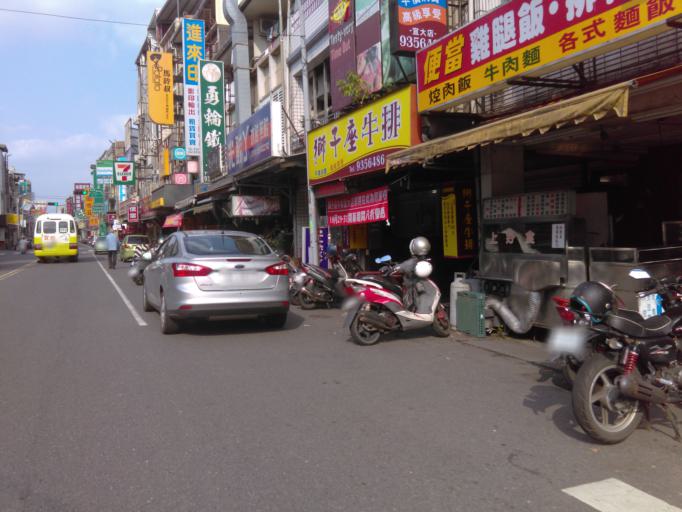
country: TW
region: Taiwan
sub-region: Yilan
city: Yilan
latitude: 24.7463
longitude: 121.7491
